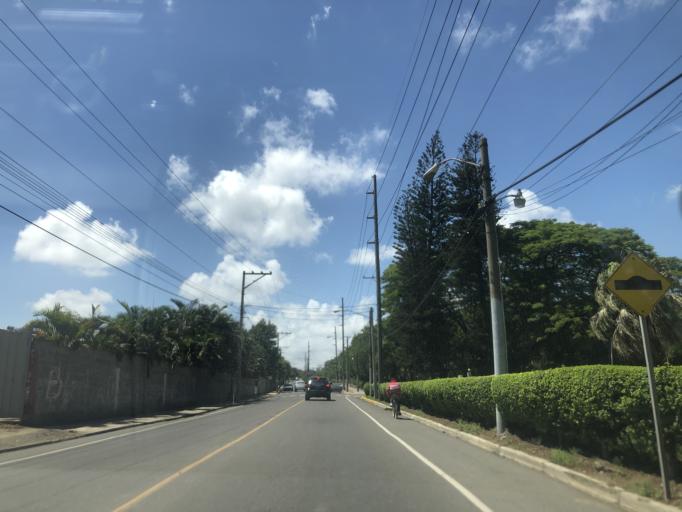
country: DO
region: Santiago
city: Santiago de los Caballeros
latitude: 19.4517
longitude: -70.7453
